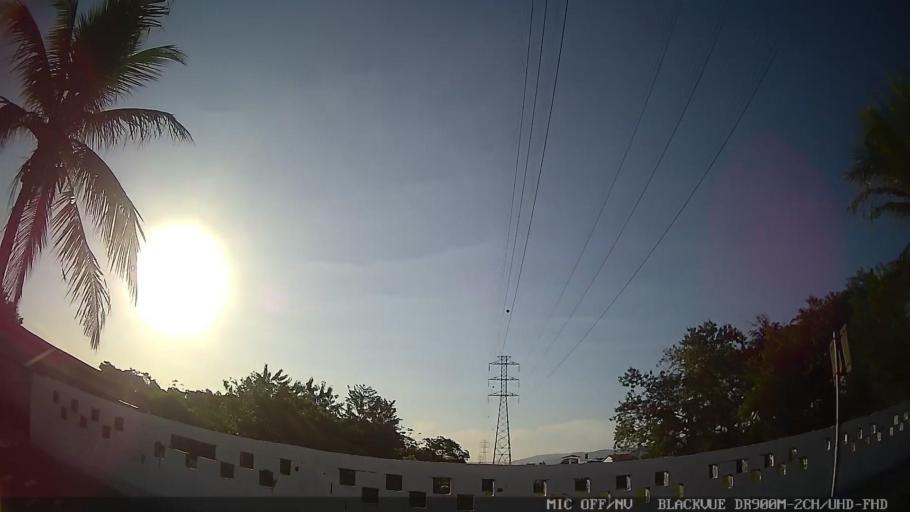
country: BR
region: Sao Paulo
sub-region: Guaruja
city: Guaruja
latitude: -23.9691
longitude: -46.2752
